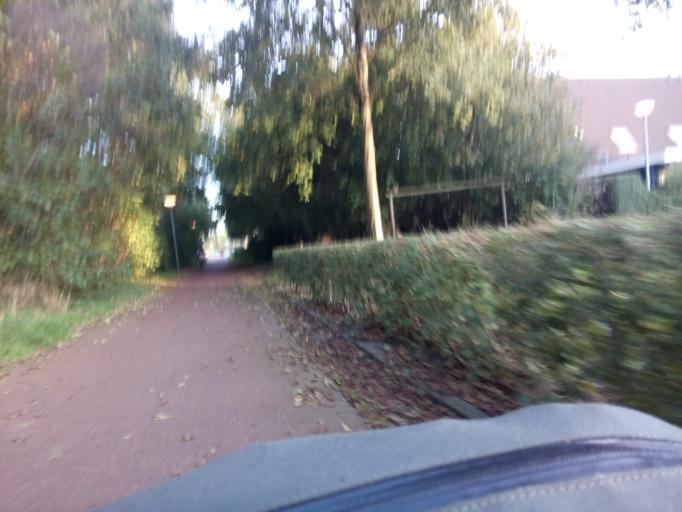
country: NL
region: Drenthe
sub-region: Gemeente Assen
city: Assen
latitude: 53.0217
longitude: 6.5686
